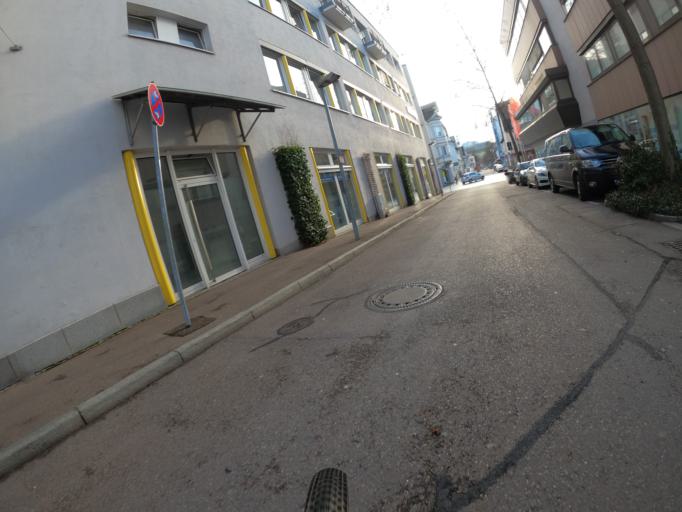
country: DE
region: Baden-Wuerttemberg
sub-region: Regierungsbezirk Stuttgart
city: Goeppingen
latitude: 48.7031
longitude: 9.6559
